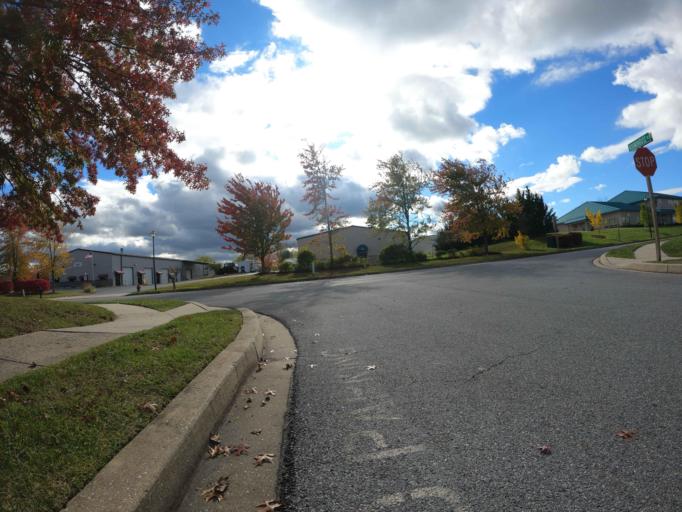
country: US
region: Maryland
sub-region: Carroll County
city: Mount Airy
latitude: 39.3684
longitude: -77.1358
